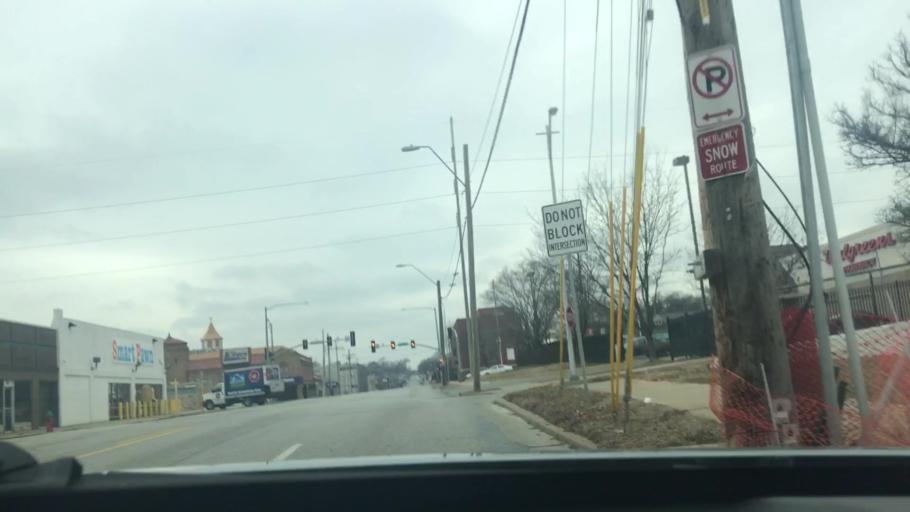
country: US
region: Kansas
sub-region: Johnson County
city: Mission Hills
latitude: 39.0133
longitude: -94.5732
